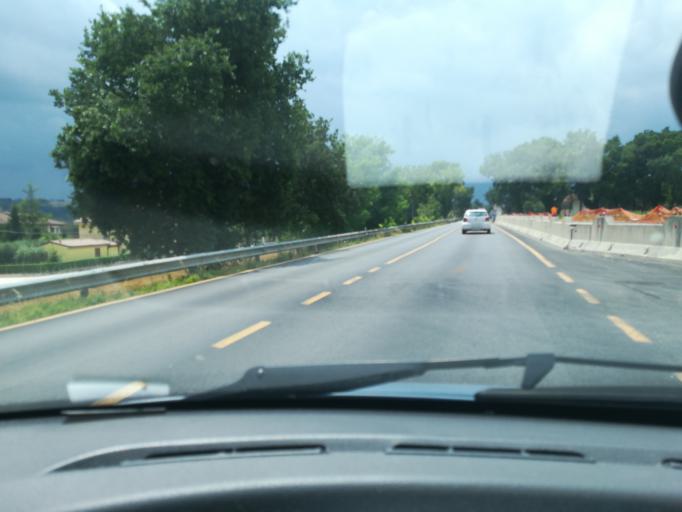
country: IT
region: The Marches
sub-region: Provincia di Macerata
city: Montecassiano
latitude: 43.3538
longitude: 13.4744
